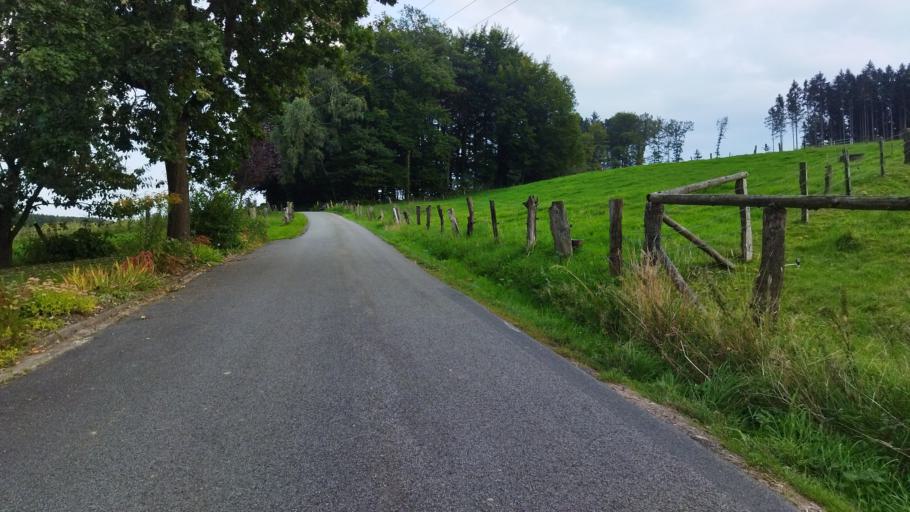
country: DE
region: Lower Saxony
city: Hagen
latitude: 52.1779
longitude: 8.0081
